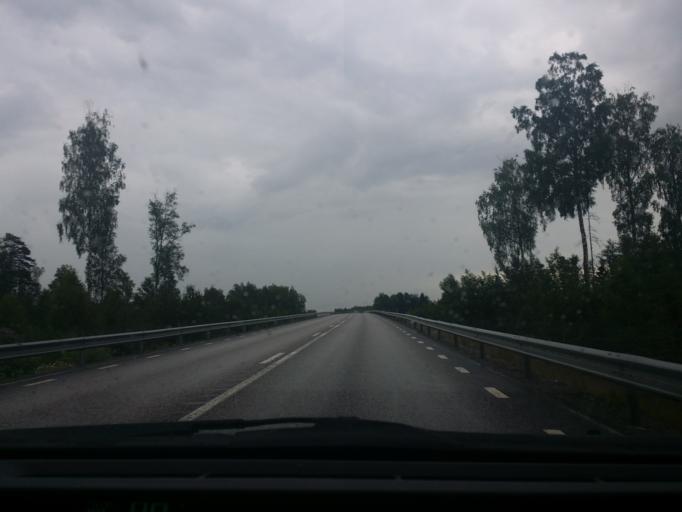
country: SE
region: OErebro
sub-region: Lindesbergs Kommun
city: Frovi
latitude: 59.4709
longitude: 15.4019
